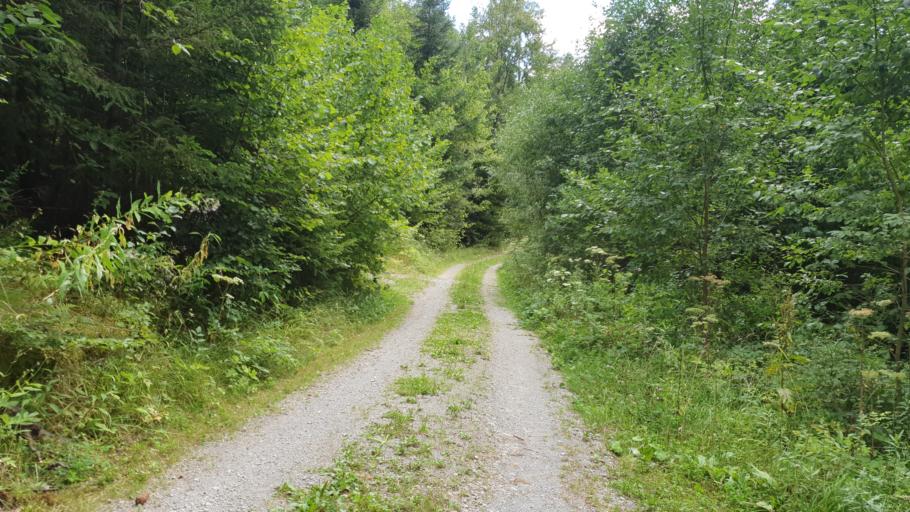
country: DE
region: Baden-Wuerttemberg
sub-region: Karlsruhe Region
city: Pfalzgrafenweiler
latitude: 48.5422
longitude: 8.5577
